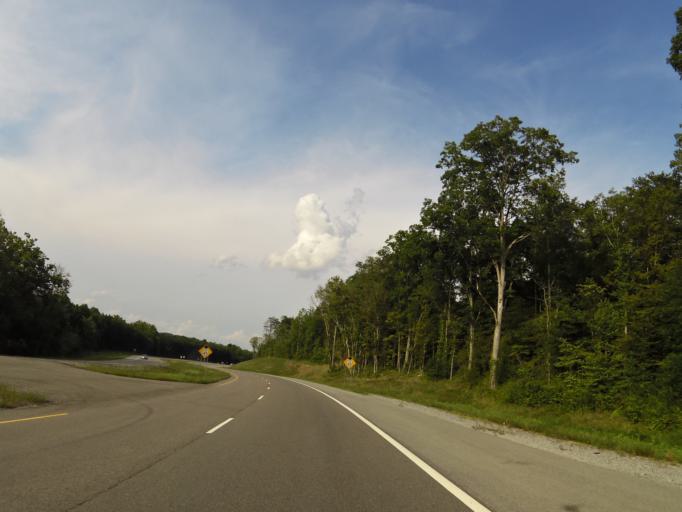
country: US
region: Tennessee
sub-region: Roane County
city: Oliver Springs
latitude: 35.9657
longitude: -84.3508
